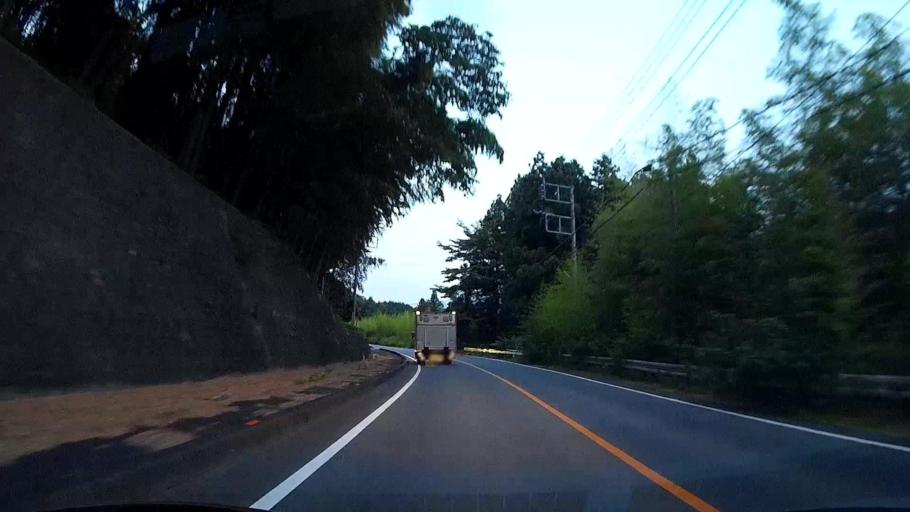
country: JP
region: Gunma
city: Annaka
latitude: 36.3890
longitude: 138.8479
